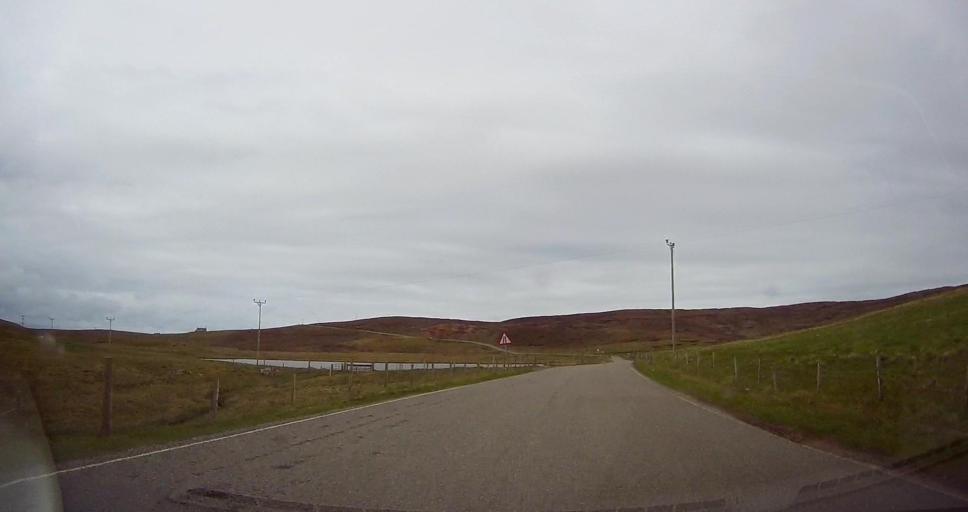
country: GB
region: Scotland
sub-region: Shetland Islands
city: Lerwick
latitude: 60.4855
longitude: -1.5062
